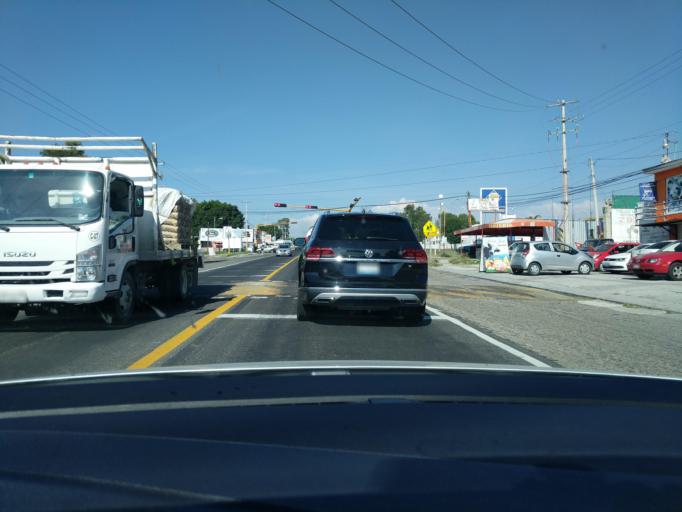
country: MX
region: Puebla
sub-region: Atlixco
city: San Agustin Huixaxtla
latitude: 18.9369
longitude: -98.4022
